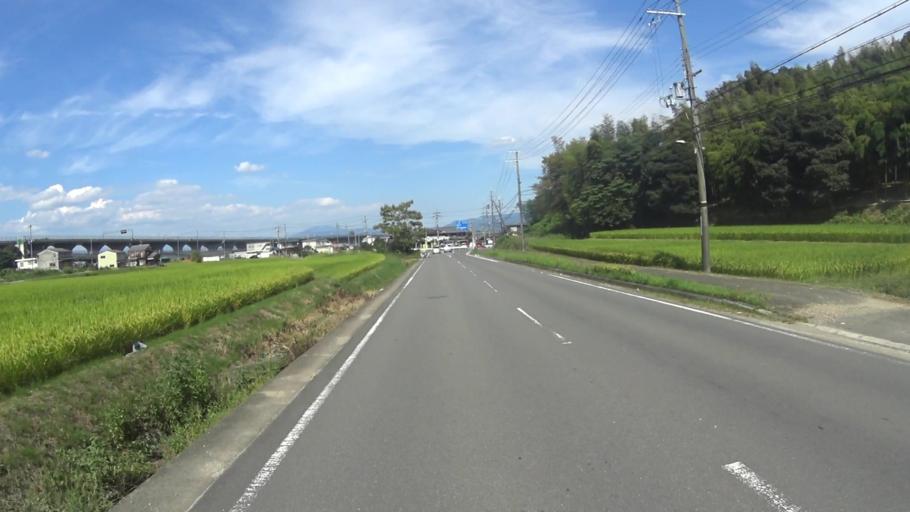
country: JP
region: Kyoto
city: Yawata
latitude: 34.8449
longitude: 135.7289
